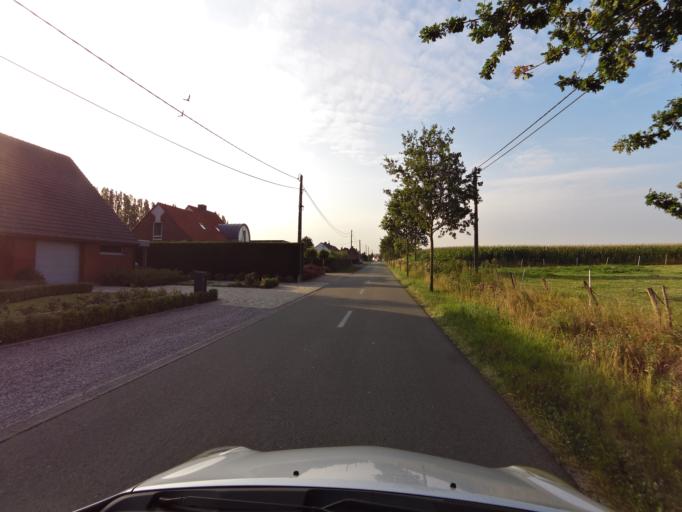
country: BE
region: Flanders
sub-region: Provincie West-Vlaanderen
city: Torhout
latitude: 51.0978
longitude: 3.0856
